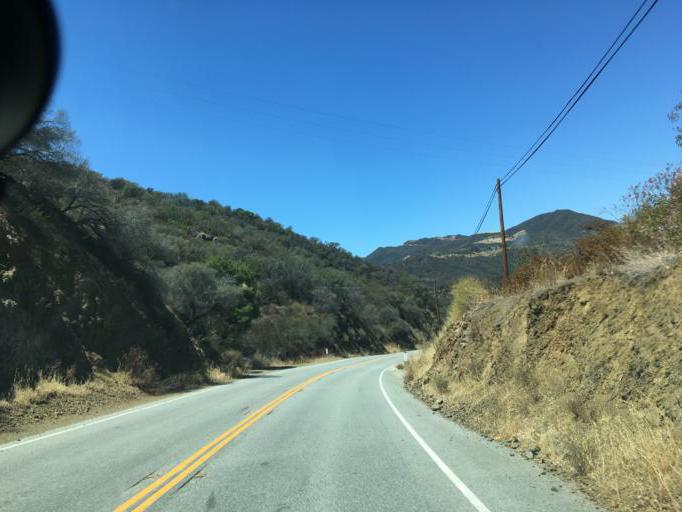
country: US
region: California
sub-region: Los Angeles County
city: Westlake Village
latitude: 34.0858
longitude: -118.8487
